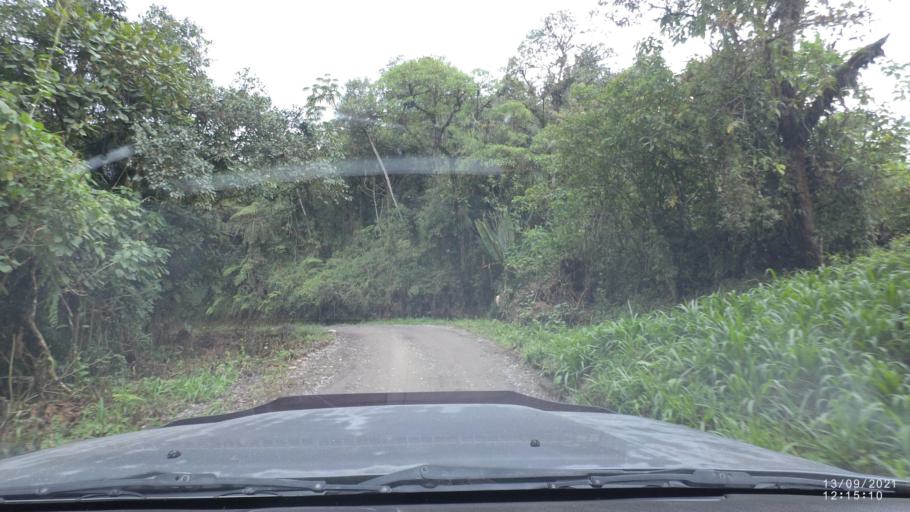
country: BO
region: Cochabamba
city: Colomi
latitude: -17.2233
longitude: -65.8237
